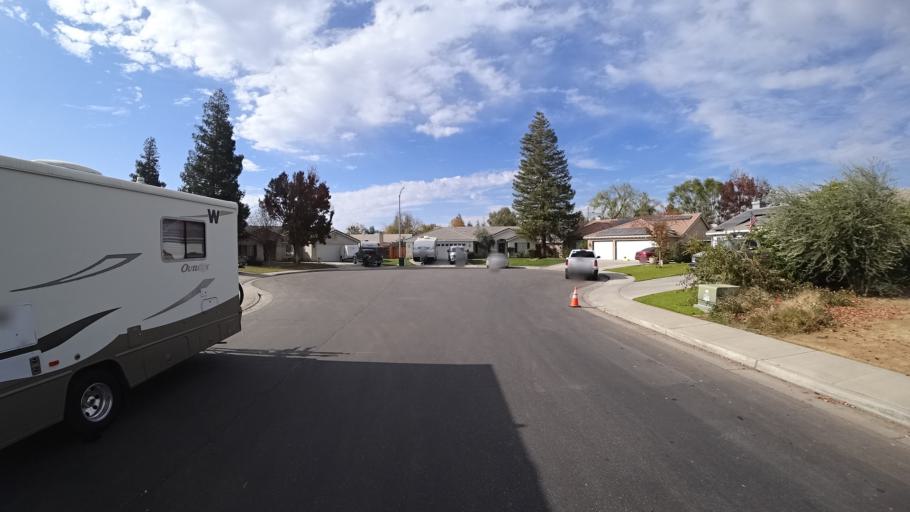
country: US
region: California
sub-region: Kern County
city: Greenacres
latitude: 35.4110
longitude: -119.1216
